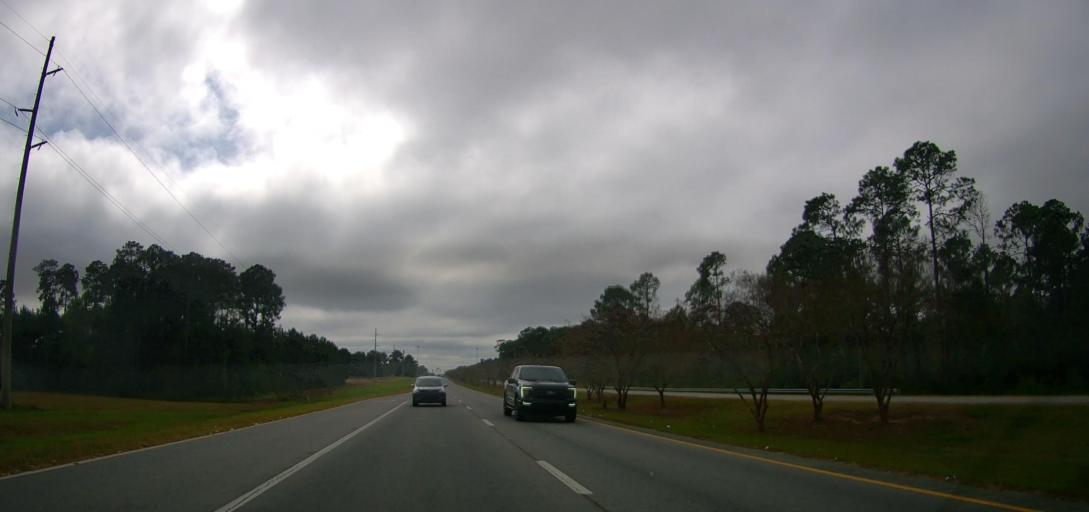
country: US
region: Georgia
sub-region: Colquitt County
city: Moultrie
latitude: 31.1200
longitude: -83.7810
